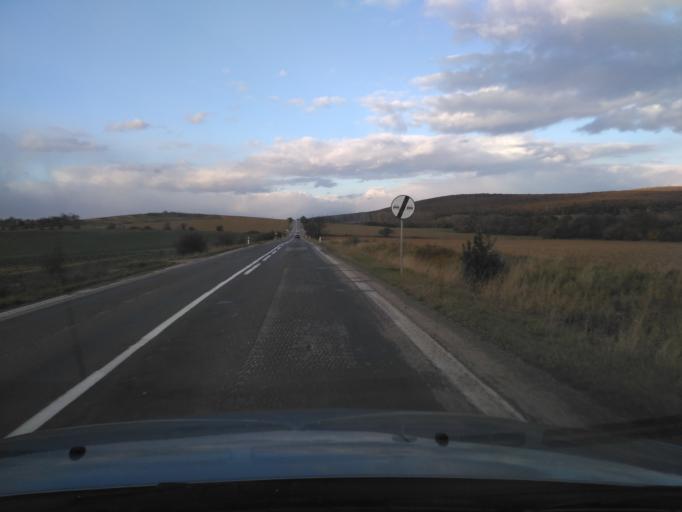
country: HU
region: Borsod-Abauj-Zemplen
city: Satoraljaujhely
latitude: 48.4786
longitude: 21.6433
